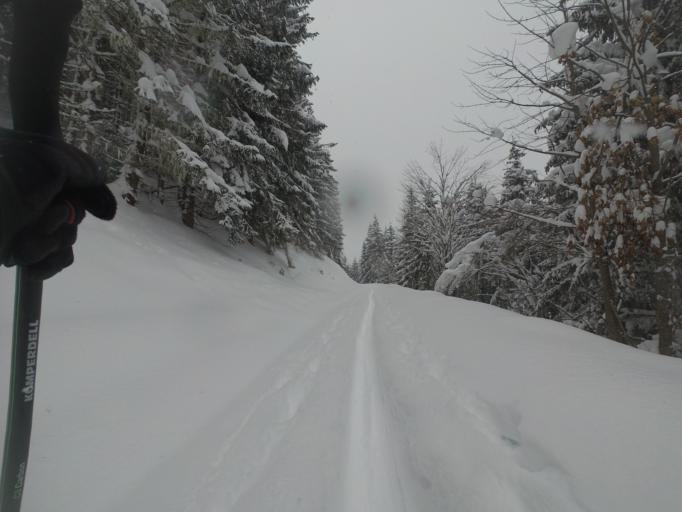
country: AT
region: Salzburg
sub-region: Politischer Bezirk Sankt Johann im Pongau
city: Sankt Johann im Pongau
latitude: 47.3135
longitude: 13.2143
